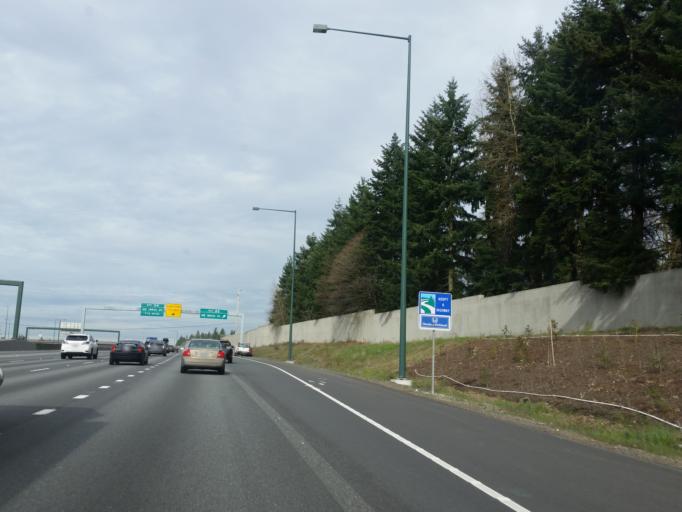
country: US
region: Washington
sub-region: King County
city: Kingsgate
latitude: 47.7387
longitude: -122.1869
